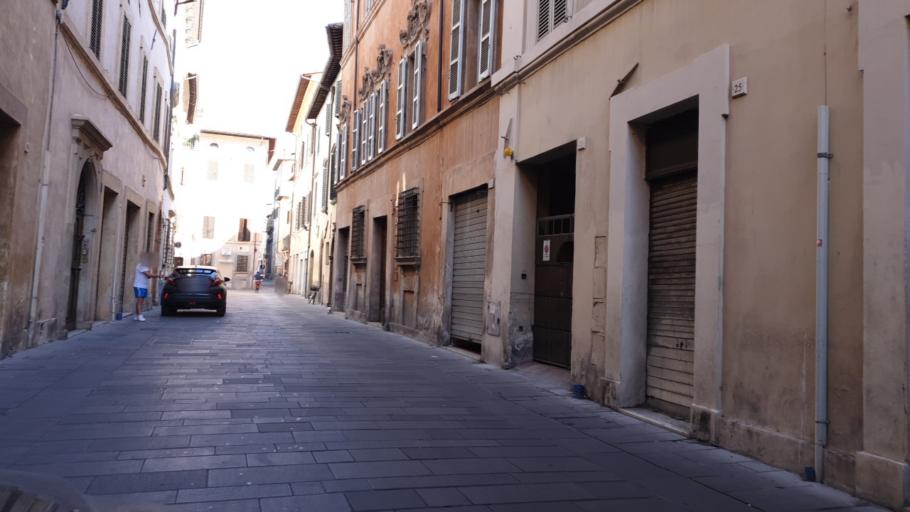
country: IT
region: Umbria
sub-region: Provincia di Perugia
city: Foligno
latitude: 42.9538
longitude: 12.7029
